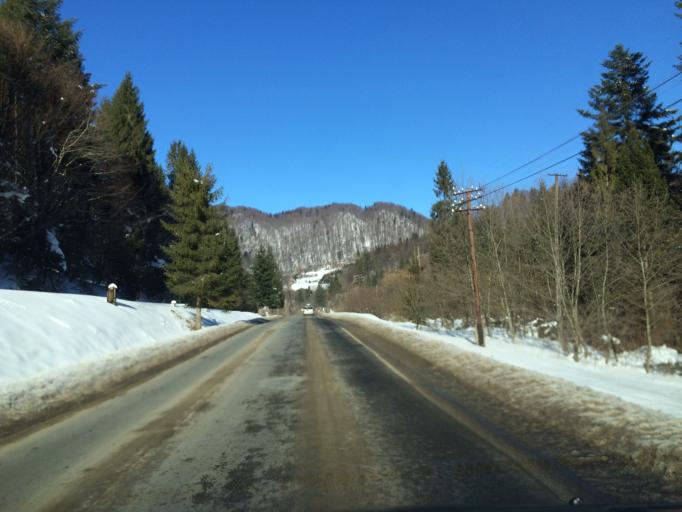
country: PL
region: Subcarpathian Voivodeship
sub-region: Powiat leski
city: Cisna
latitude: 49.2187
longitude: 22.3649
